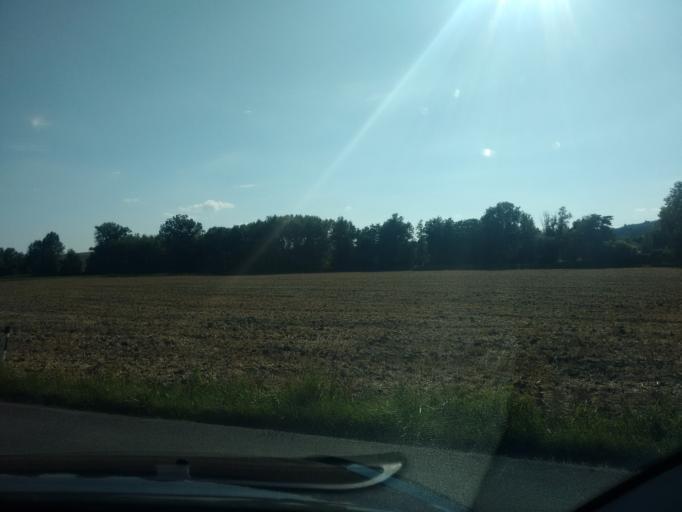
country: AT
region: Upper Austria
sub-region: Wels-Land
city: Buchkirchen
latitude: 48.2391
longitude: 13.9739
